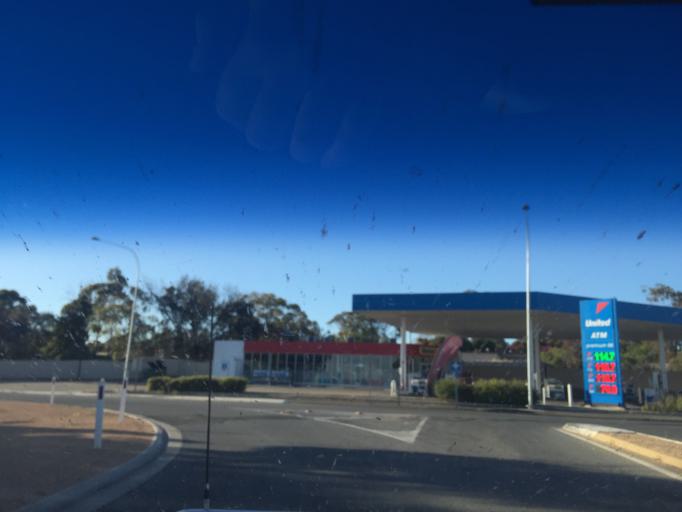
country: AU
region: South Australia
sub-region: Berri and Barmera
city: Berri
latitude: -34.2837
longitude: 140.5964
